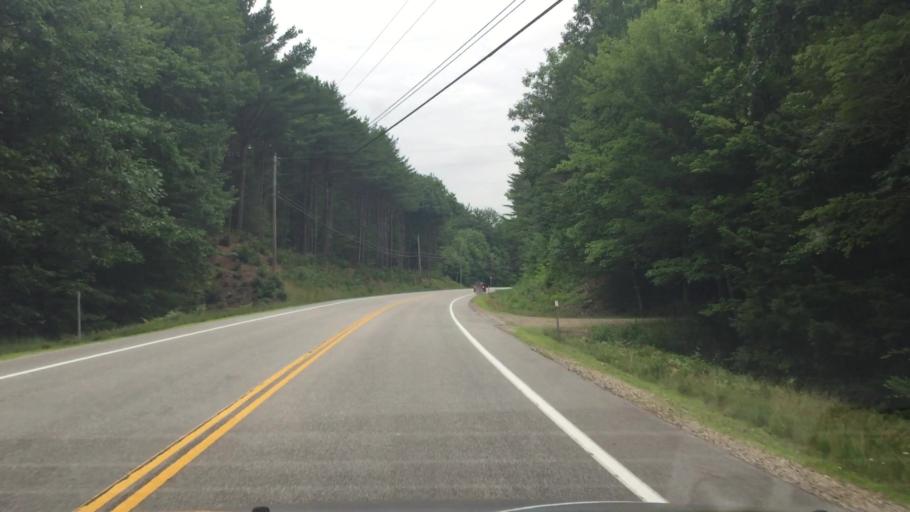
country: US
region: New Hampshire
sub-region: Carroll County
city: Sandwich
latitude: 43.7961
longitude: -71.3714
